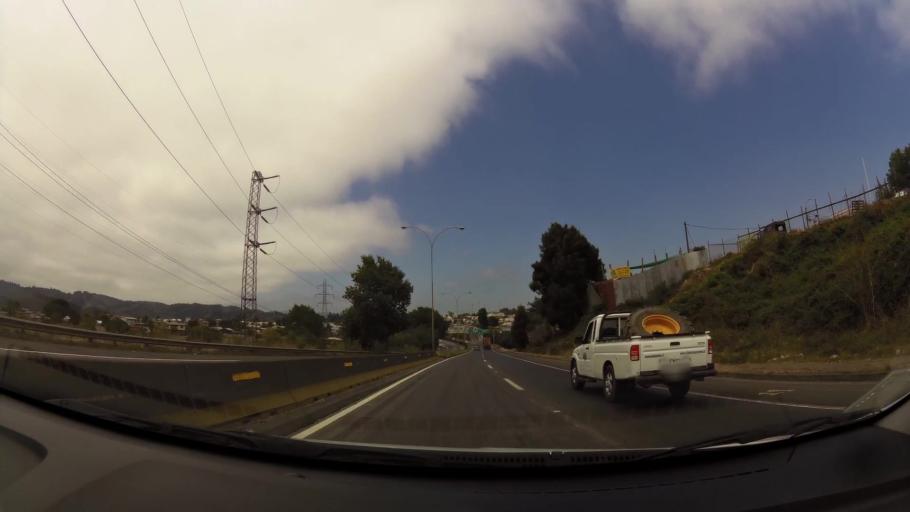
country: CL
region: Biobio
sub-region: Provincia de Concepcion
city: Concepcion
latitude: -36.8002
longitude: -73.0435
